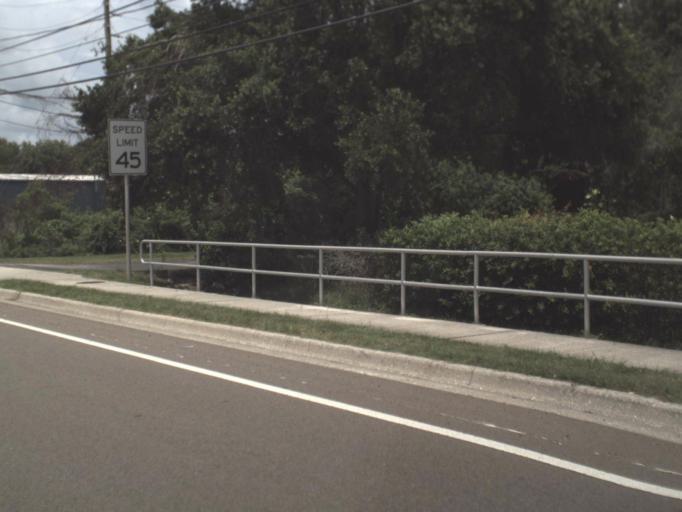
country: US
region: Florida
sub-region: Pinellas County
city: Saint George
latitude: 28.0490
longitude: -82.7404
